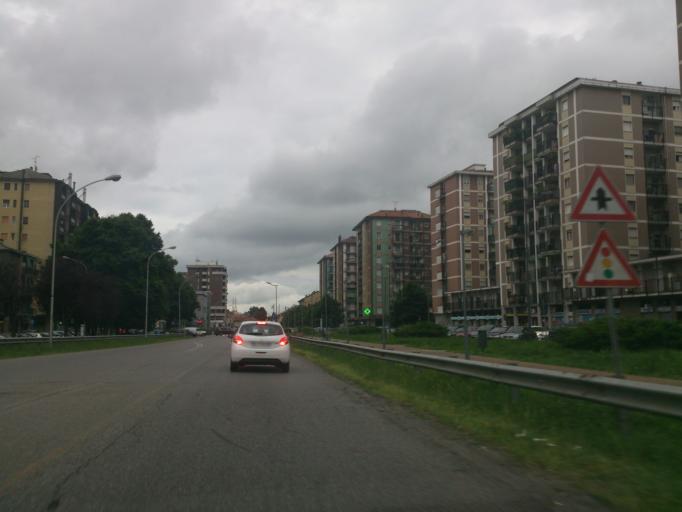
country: IT
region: Lombardy
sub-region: Citta metropolitana di Milano
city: San Giuliano Milanese
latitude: 45.3976
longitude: 9.2811
